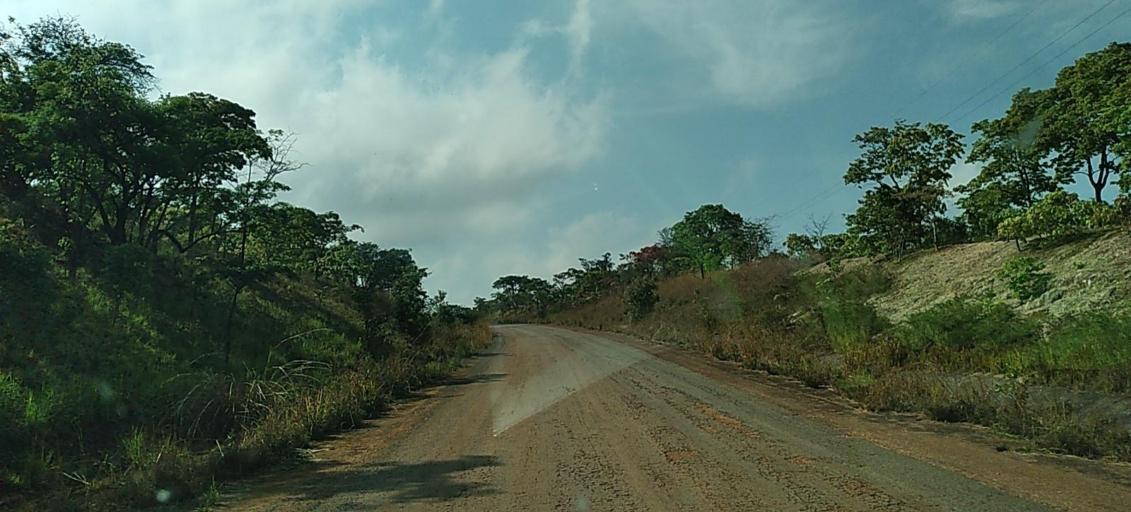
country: ZM
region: North-Western
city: Mwinilunga
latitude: -11.7615
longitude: 24.9971
